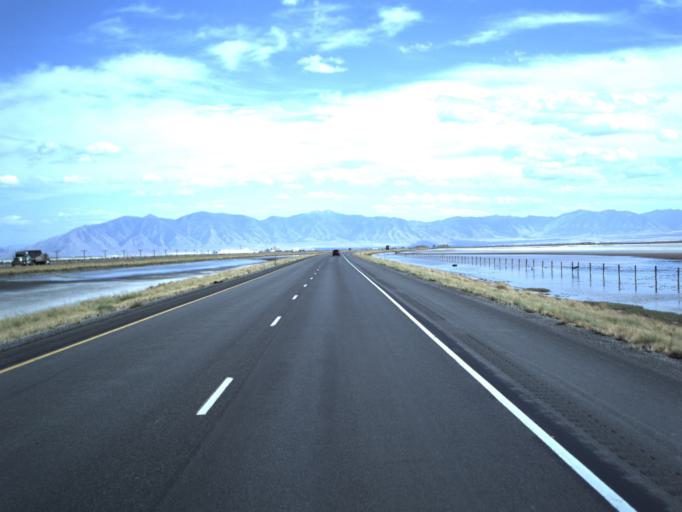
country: US
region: Utah
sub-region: Tooele County
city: Grantsville
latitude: 40.7213
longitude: -112.5595
